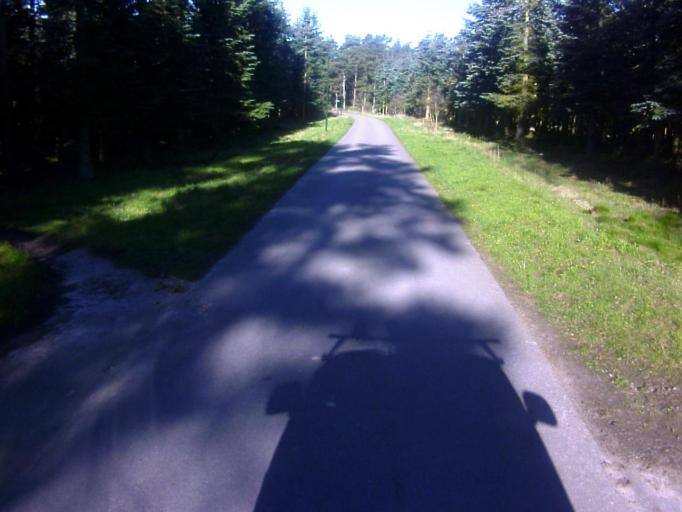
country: SE
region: Skane
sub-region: Kavlinge Kommun
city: Hofterup
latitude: 55.8177
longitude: 12.9685
